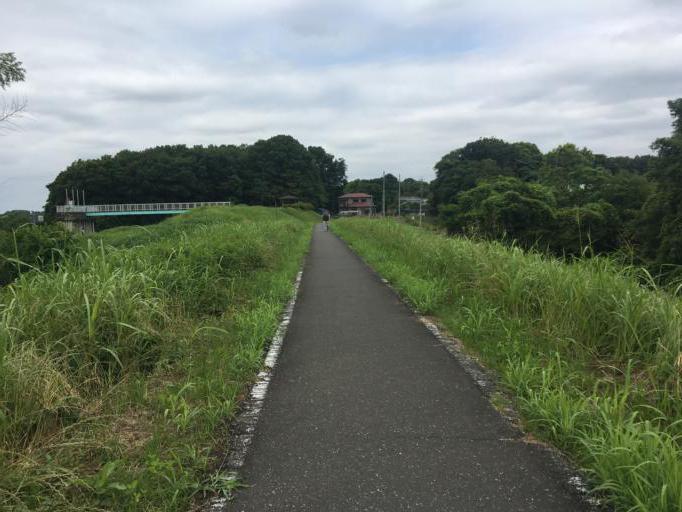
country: JP
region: Saitama
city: Okegawa
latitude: 35.9522
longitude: 139.5468
